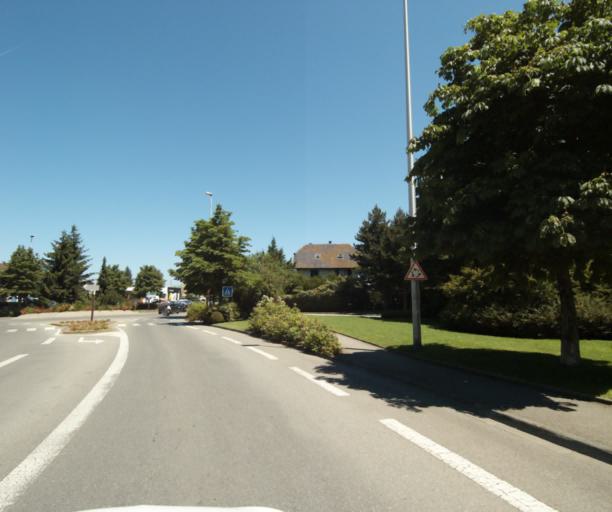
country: FR
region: Rhone-Alpes
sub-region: Departement de la Haute-Savoie
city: Thonon-les-Bains
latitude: 46.3776
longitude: 6.4902
